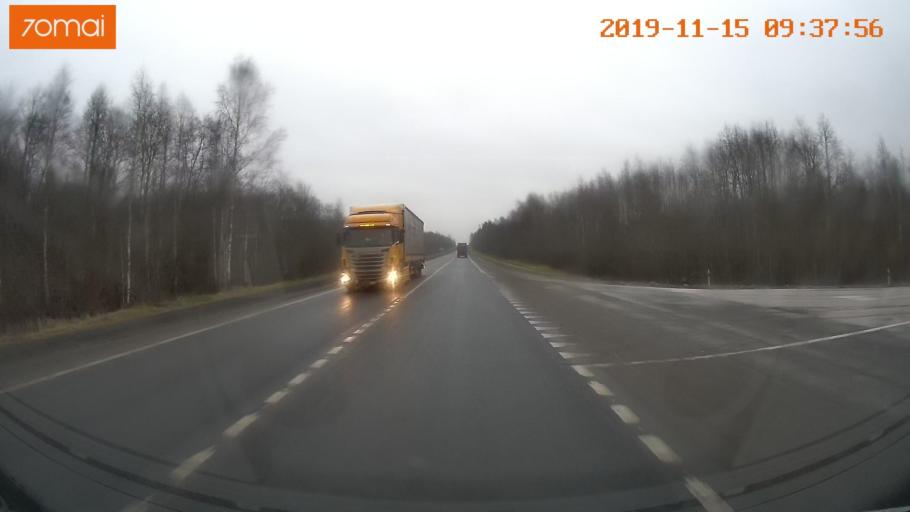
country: RU
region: Vologda
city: Sheksna
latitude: 59.2365
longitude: 38.4460
